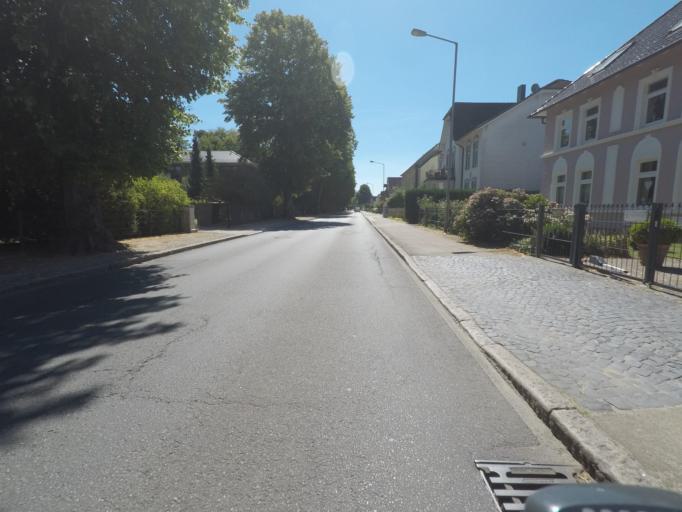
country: DE
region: Schleswig-Holstein
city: Trittau
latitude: 53.6185
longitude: 10.4028
